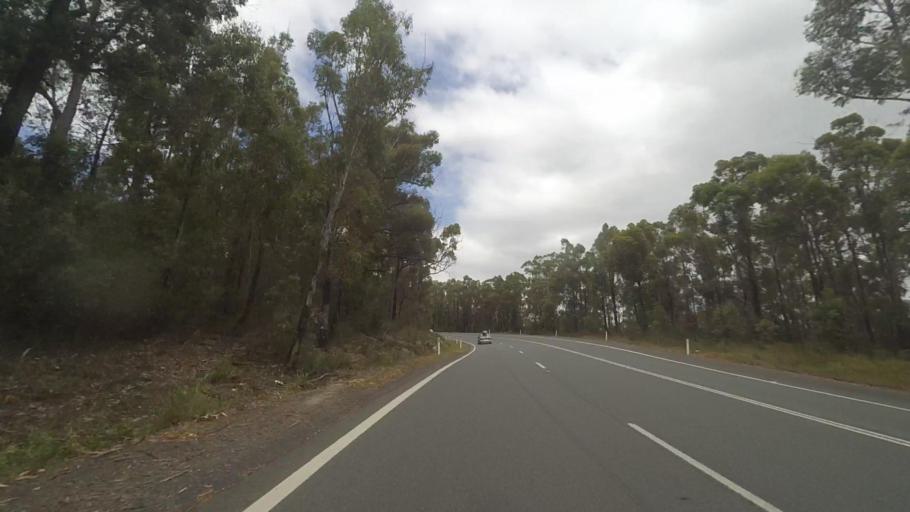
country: AU
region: New South Wales
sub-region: Shoalhaven Shire
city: Milton
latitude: -35.1391
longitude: 150.4649
